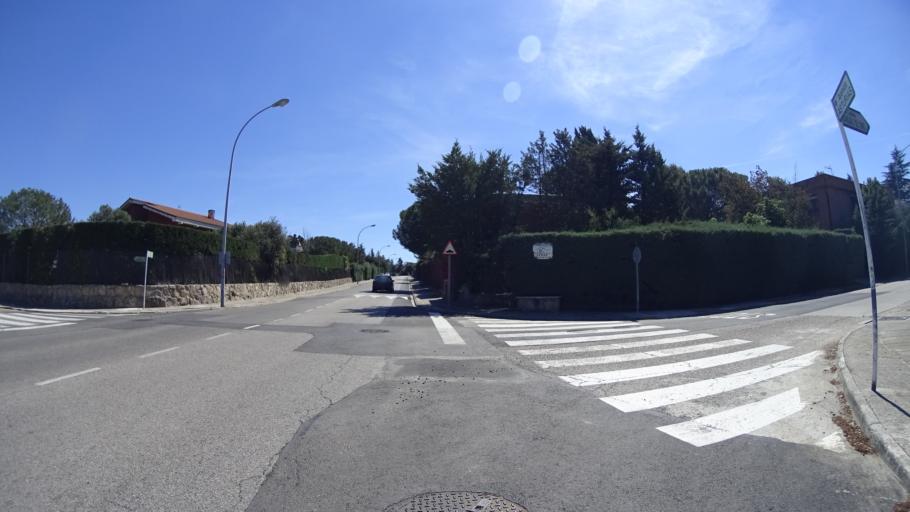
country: ES
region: Madrid
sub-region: Provincia de Madrid
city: Torrelodones
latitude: 40.6011
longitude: -3.9435
